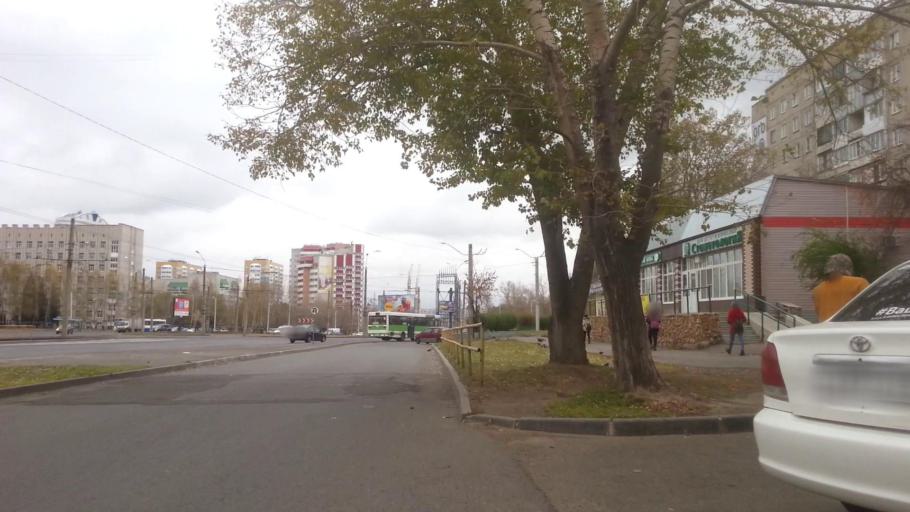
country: RU
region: Altai Krai
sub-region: Gorod Barnaulskiy
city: Barnaul
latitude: 53.3666
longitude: 83.7068
